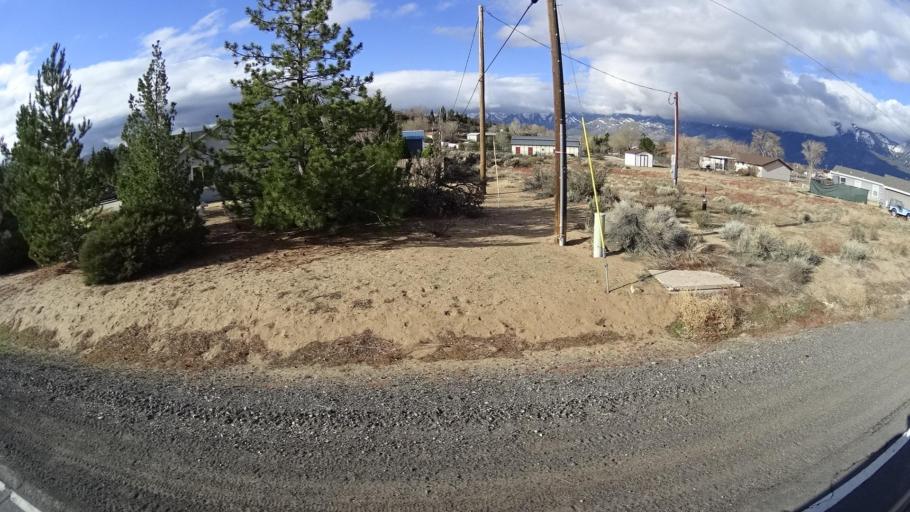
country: US
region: Nevada
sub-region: Storey County
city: Virginia City
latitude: 39.2894
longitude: -119.7660
